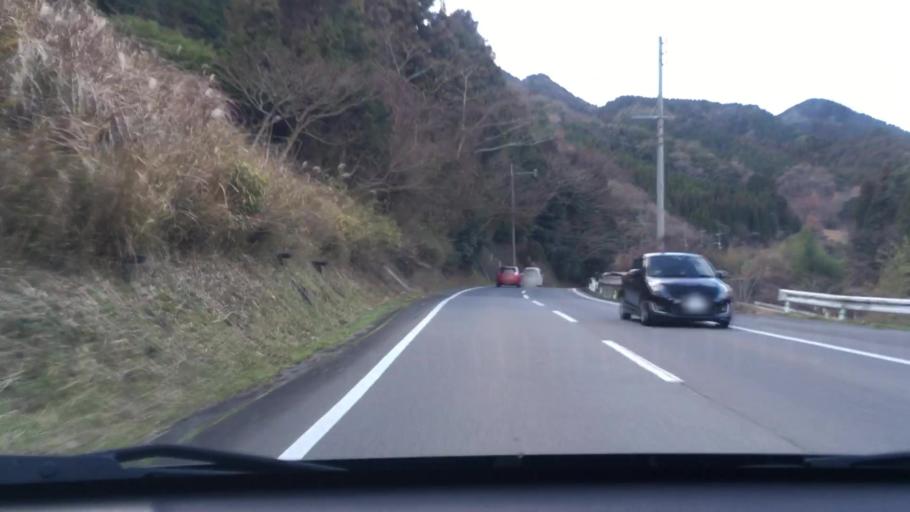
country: JP
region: Oita
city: Bungo-Takada-shi
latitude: 33.4686
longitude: 131.3874
